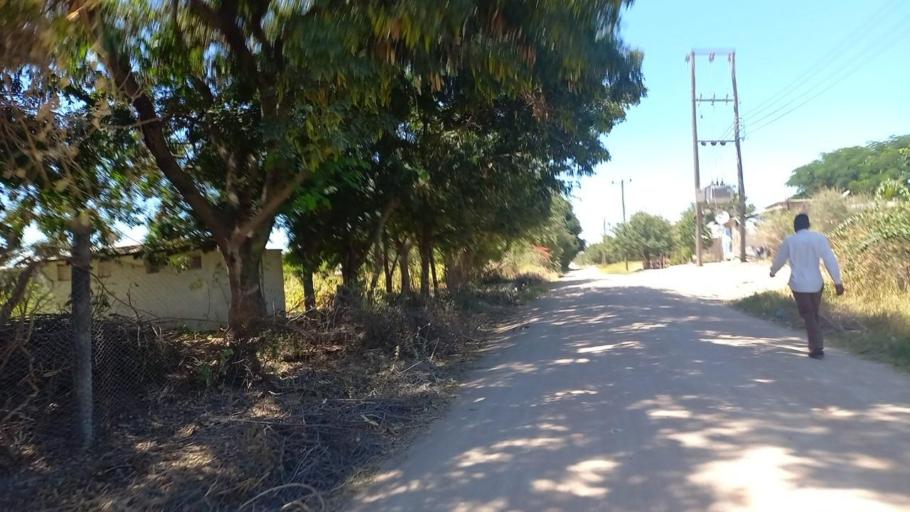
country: TZ
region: Dodoma
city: Dodoma
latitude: -6.1300
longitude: 35.7379
